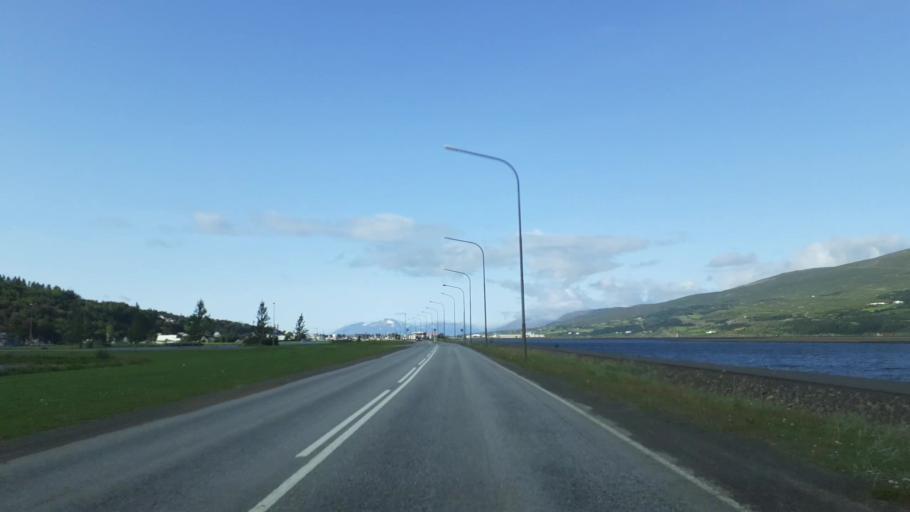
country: IS
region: Northeast
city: Akureyri
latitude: 65.6634
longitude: -18.0797
